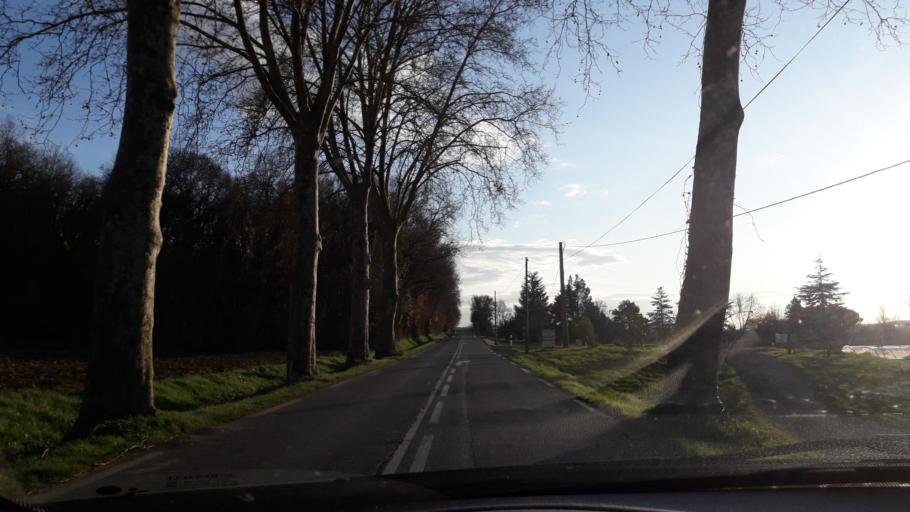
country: FR
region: Midi-Pyrenees
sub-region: Departement de la Haute-Garonne
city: Daux
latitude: 43.7125
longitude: 1.2476
